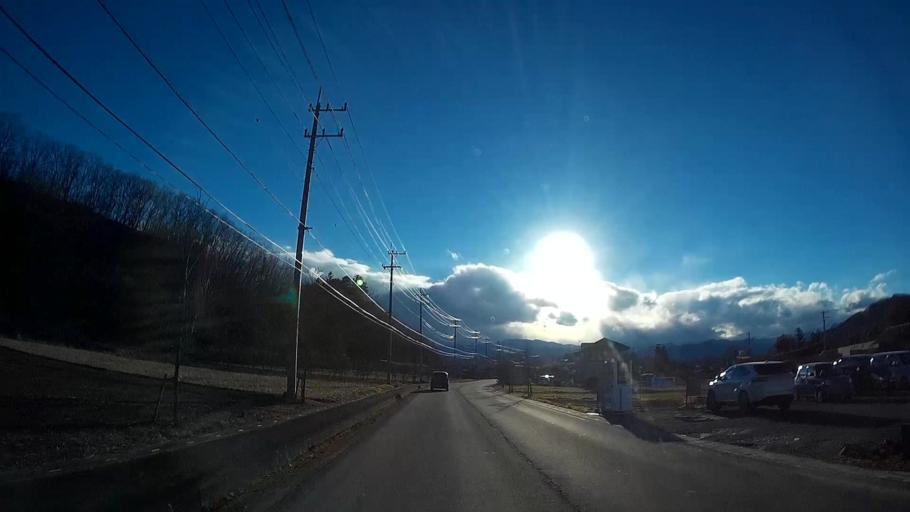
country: JP
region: Saitama
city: Chichibu
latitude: 36.0520
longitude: 139.0531
